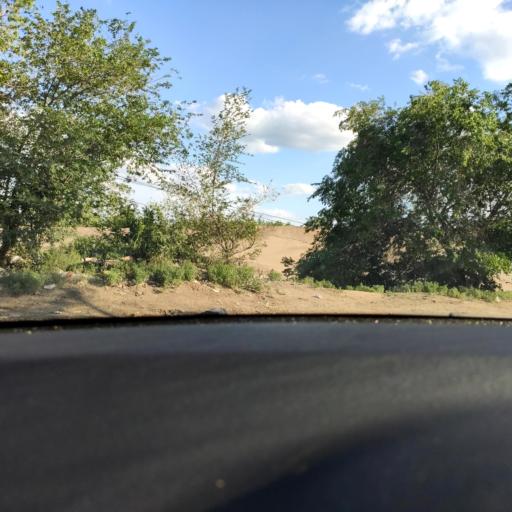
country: RU
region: Samara
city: Smyshlyayevka
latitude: 53.1818
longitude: 50.2966
